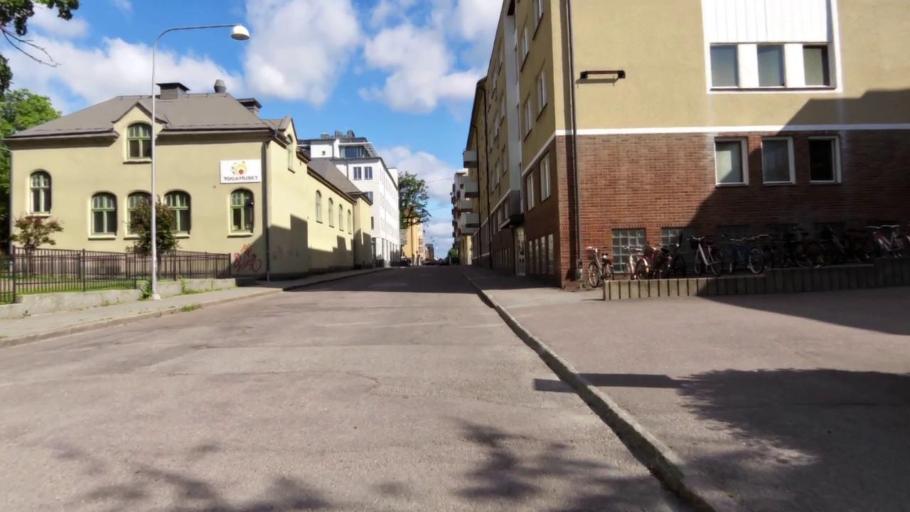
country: SE
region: OEstergoetland
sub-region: Linkopings Kommun
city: Linkoping
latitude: 58.4080
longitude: 15.6301
